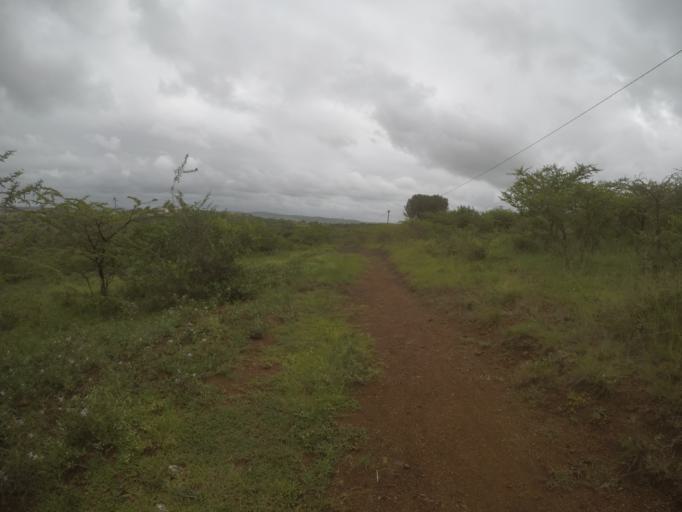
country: ZA
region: KwaZulu-Natal
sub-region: uThungulu District Municipality
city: Empangeni
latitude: -28.6029
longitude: 31.8536
